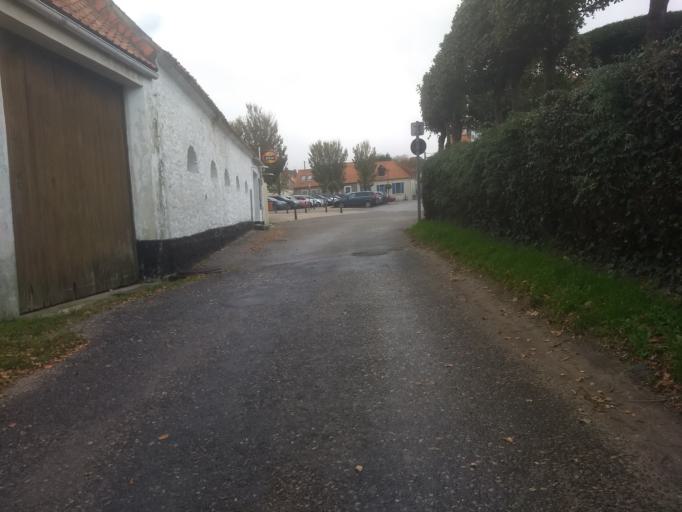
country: FR
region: Nord-Pas-de-Calais
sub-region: Departement du Pas-de-Calais
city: Wissant
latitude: 50.8858
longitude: 1.6617
